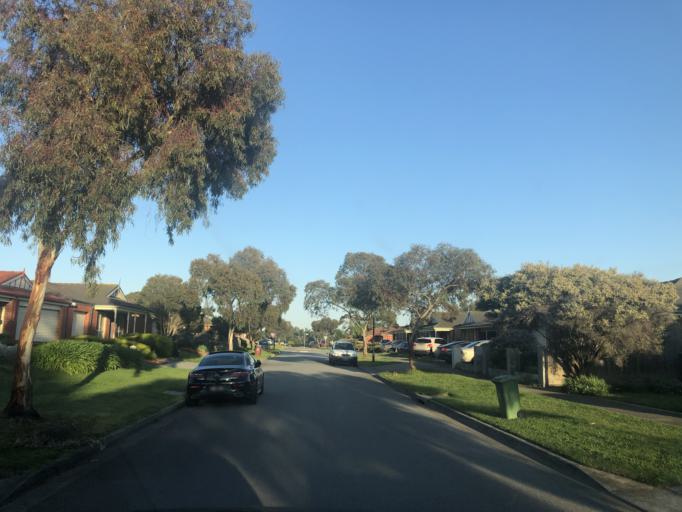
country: AU
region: Victoria
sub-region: Casey
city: Hampton Park
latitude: -38.0408
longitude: 145.2609
